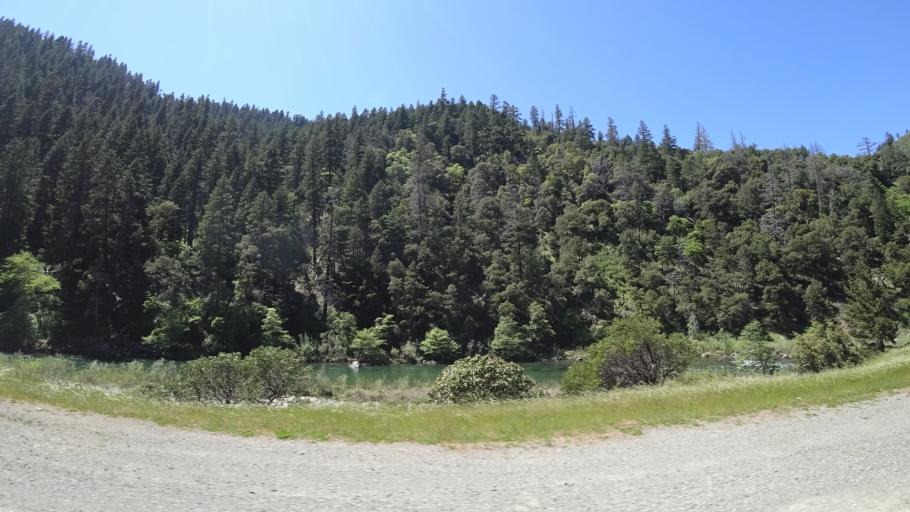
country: US
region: California
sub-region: Trinity County
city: Hayfork
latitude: 40.7740
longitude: -123.3118
